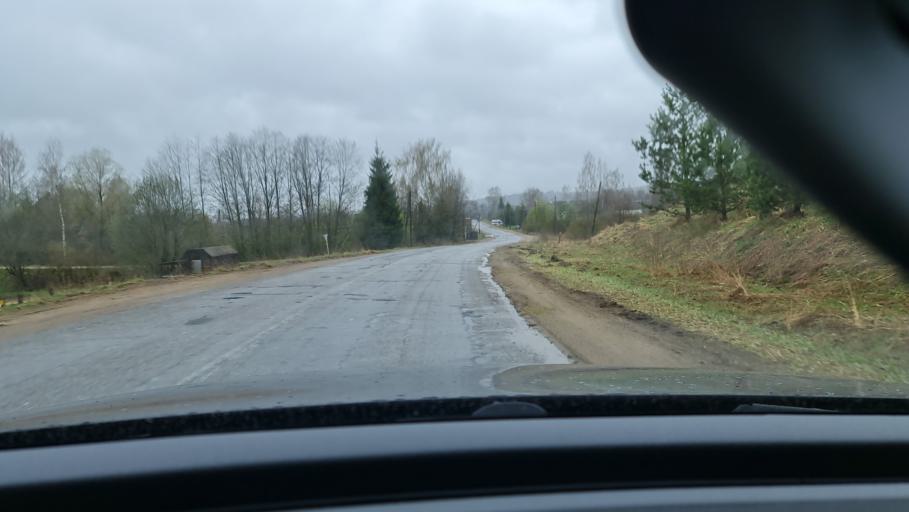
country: RU
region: Novgorod
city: Valday
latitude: 58.0319
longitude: 32.9707
